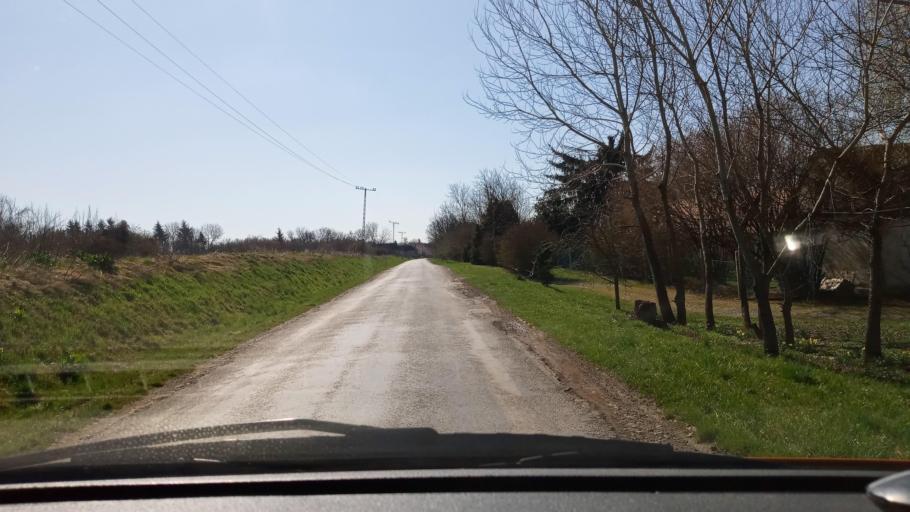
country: HU
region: Baranya
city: Kozarmisleny
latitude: 46.0654
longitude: 18.3712
